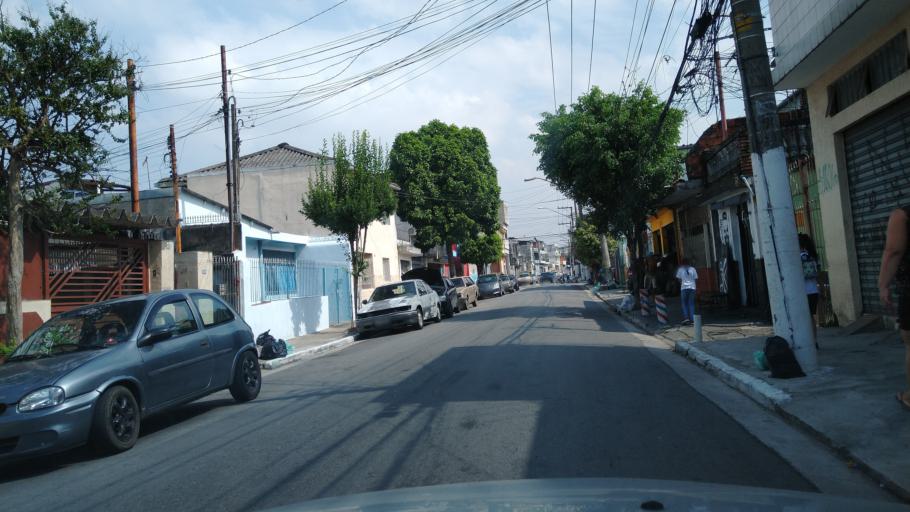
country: BR
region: Sao Paulo
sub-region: Guarulhos
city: Guarulhos
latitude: -23.4743
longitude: -46.5769
